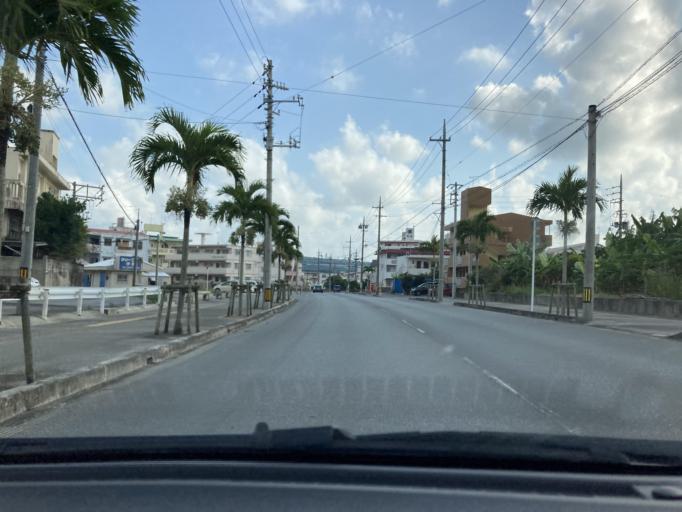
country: JP
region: Okinawa
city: Tomigusuku
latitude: 26.1536
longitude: 127.7176
